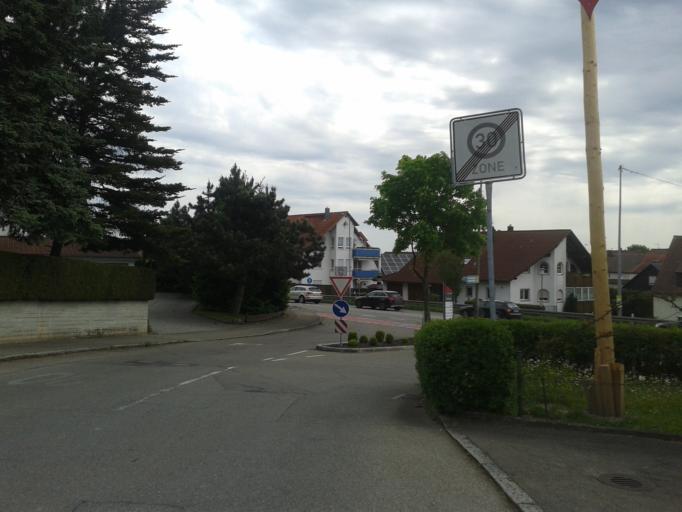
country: DE
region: Baden-Wuerttemberg
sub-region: Tuebingen Region
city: Erbach
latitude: 48.3207
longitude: 9.8855
